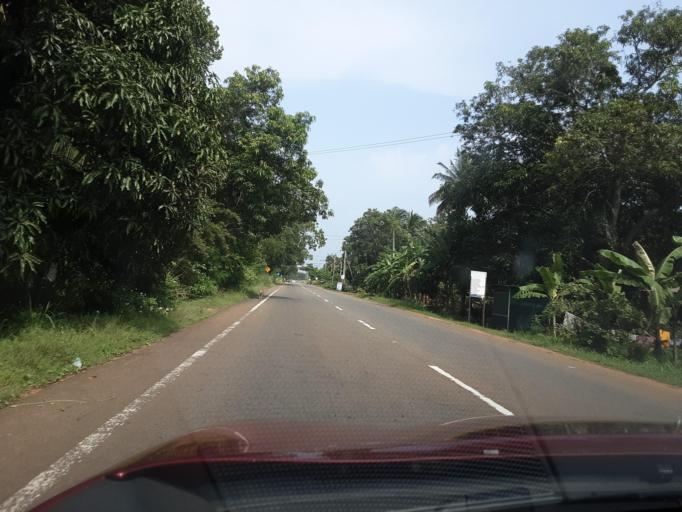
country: LK
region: North Central
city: Anuradhapura
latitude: 8.3298
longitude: 80.5011
